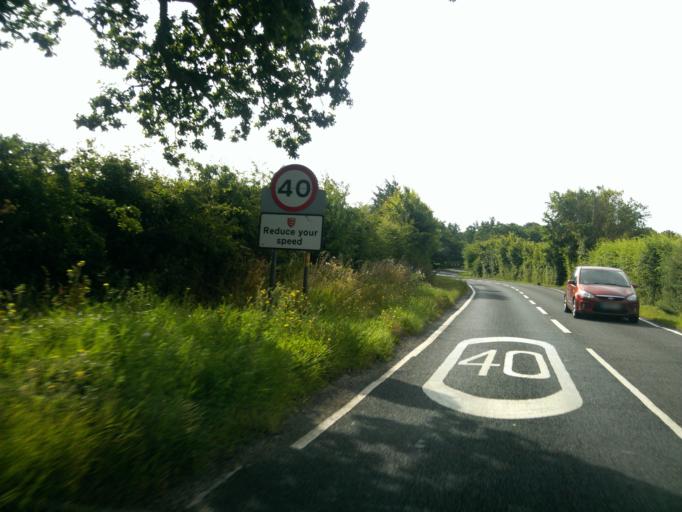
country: GB
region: England
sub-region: Essex
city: Great Bentley
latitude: 51.8310
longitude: 1.0640
